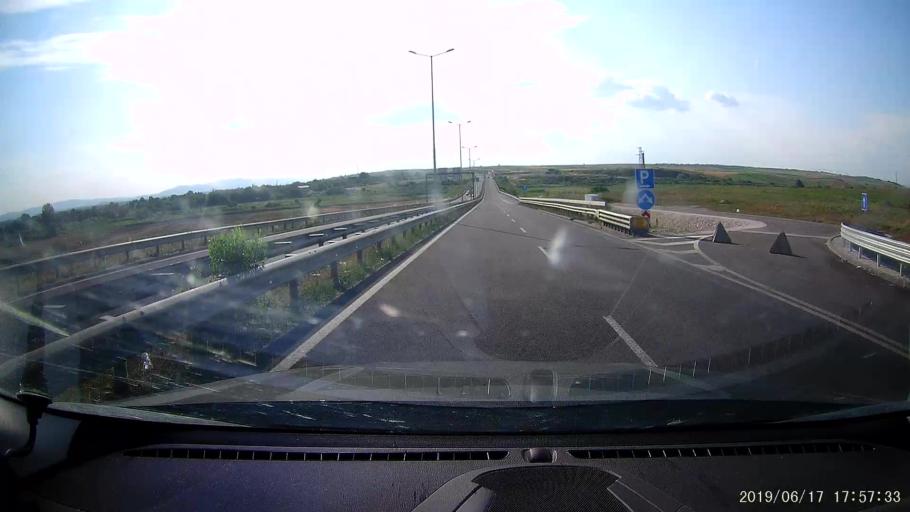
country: GR
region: East Macedonia and Thrace
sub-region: Nomos Evrou
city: Rizia
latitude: 41.7216
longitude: 26.3339
